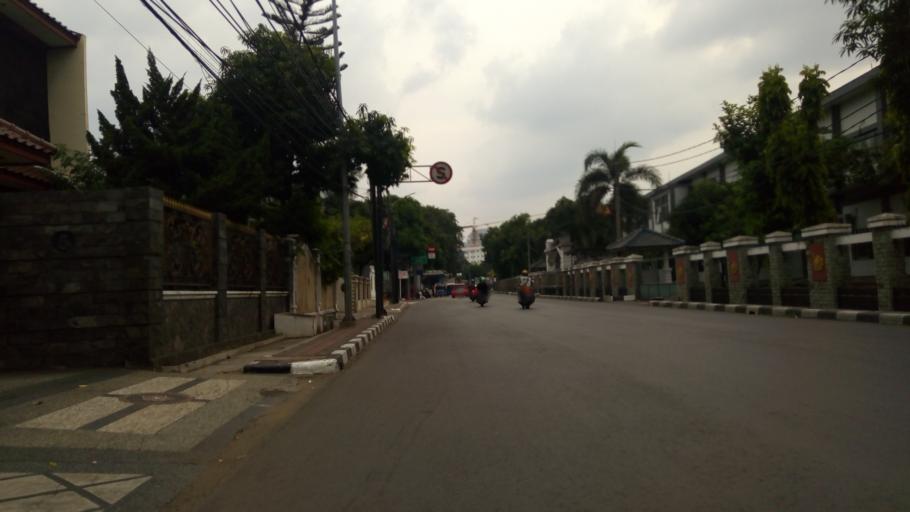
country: ID
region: Jakarta Raya
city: Jakarta
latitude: -6.1747
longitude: 106.8377
